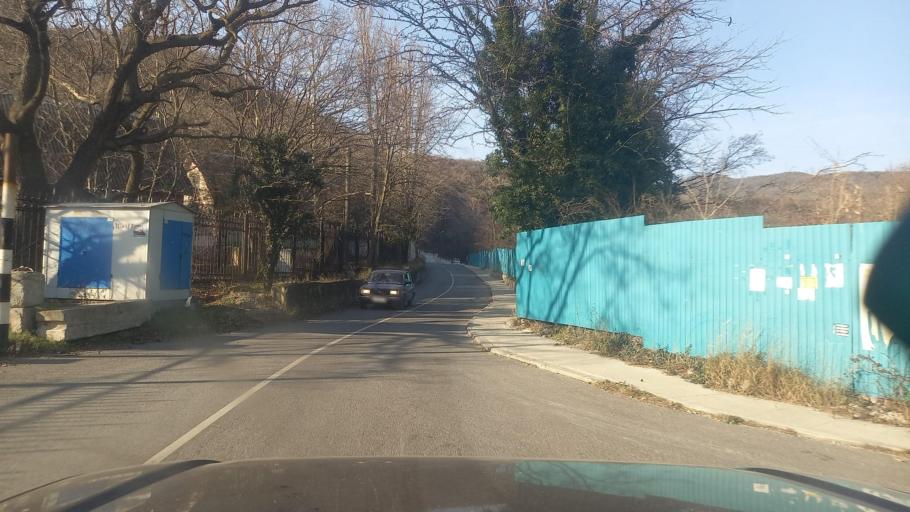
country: RU
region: Krasnodarskiy
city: Myskhako
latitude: 44.6592
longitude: 37.6868
